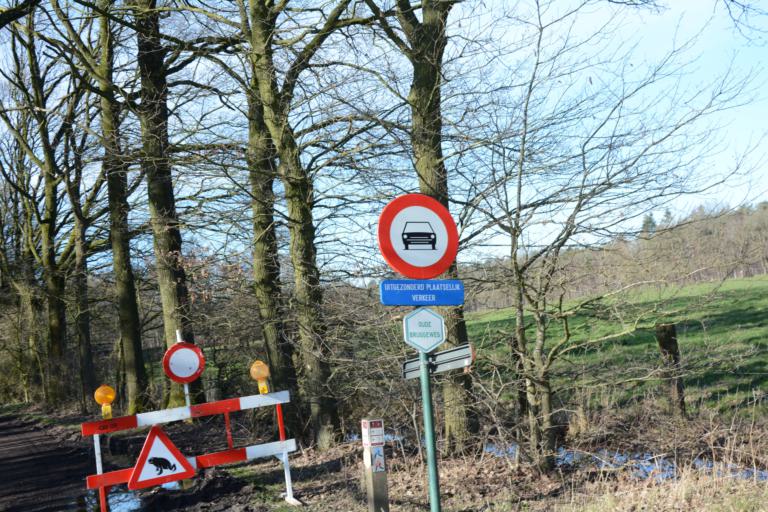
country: BE
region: Flanders
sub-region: Provincie Oost-Vlaanderen
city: Knesselare
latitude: 51.1500
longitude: 3.4487
